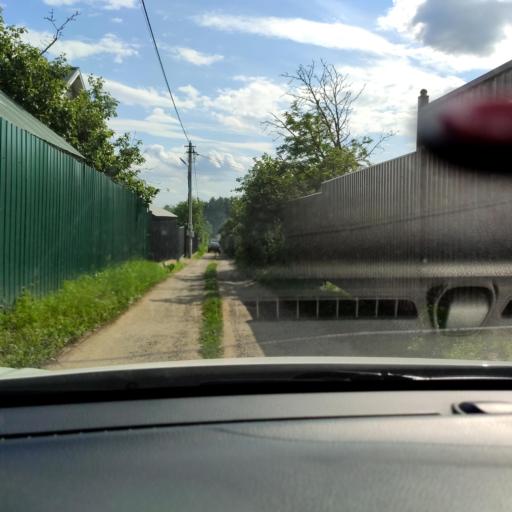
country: RU
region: Tatarstan
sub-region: Gorod Kazan'
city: Kazan
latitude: 55.8900
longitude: 49.0585
